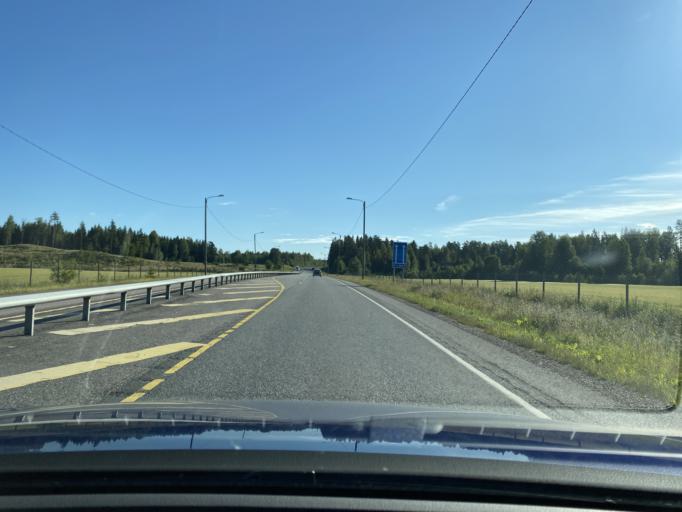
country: FI
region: Haeme
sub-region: Riihimaeki
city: Loppi
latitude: 60.7176
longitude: 24.4915
